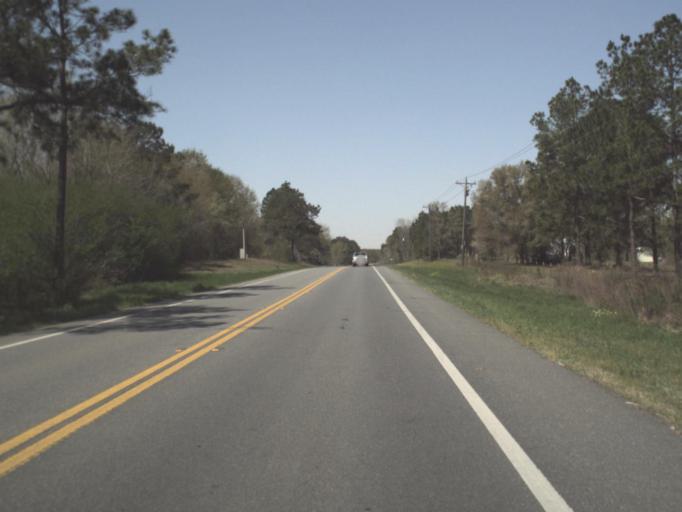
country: US
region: Florida
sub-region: Jackson County
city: Graceville
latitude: 30.9644
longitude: -85.5951
